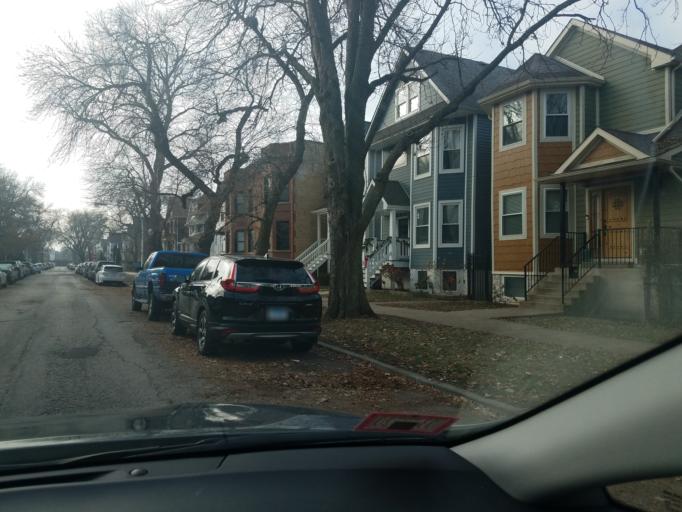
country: US
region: Illinois
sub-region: Cook County
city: Lincolnwood
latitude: 41.9421
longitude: -87.7052
